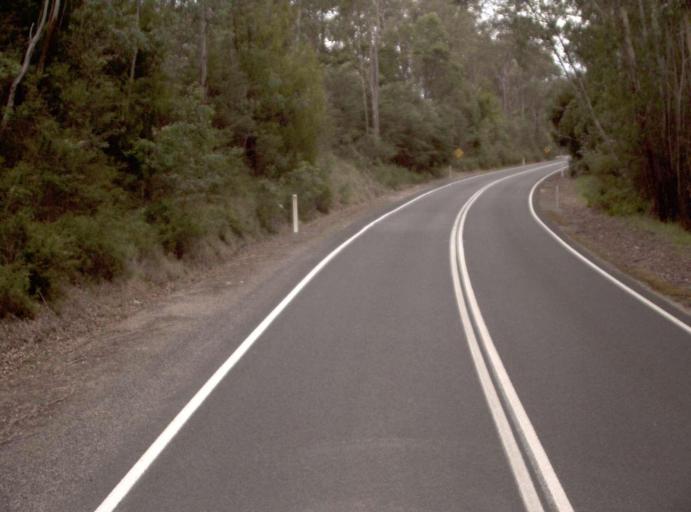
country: AU
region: New South Wales
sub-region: Bombala
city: Bombala
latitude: -37.3384
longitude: 149.2062
